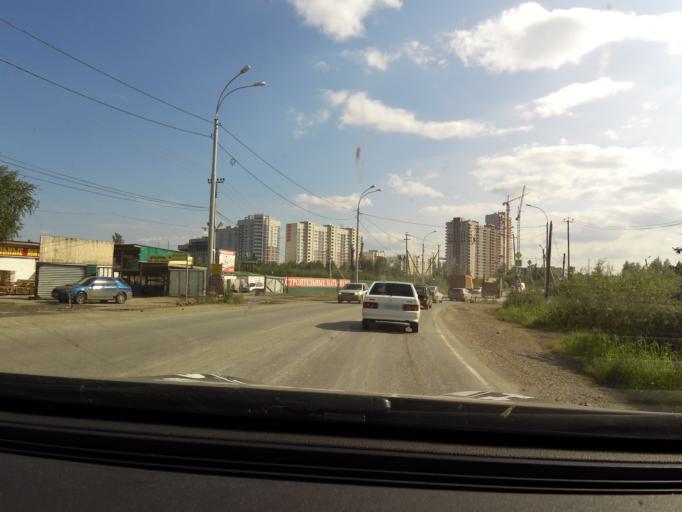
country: RU
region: Sverdlovsk
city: Shirokaya Rechka
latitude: 56.7996
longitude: 60.4948
